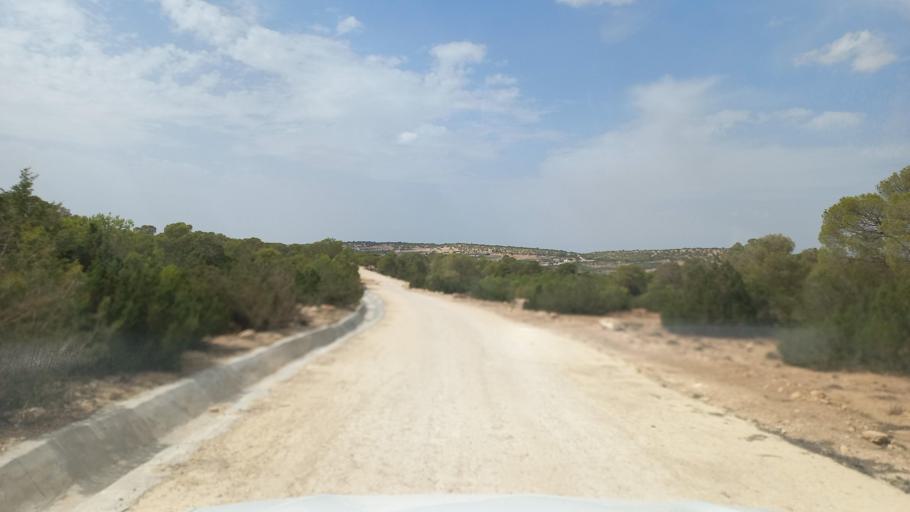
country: TN
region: Al Qasrayn
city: Kasserine
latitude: 35.3831
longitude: 8.8740
